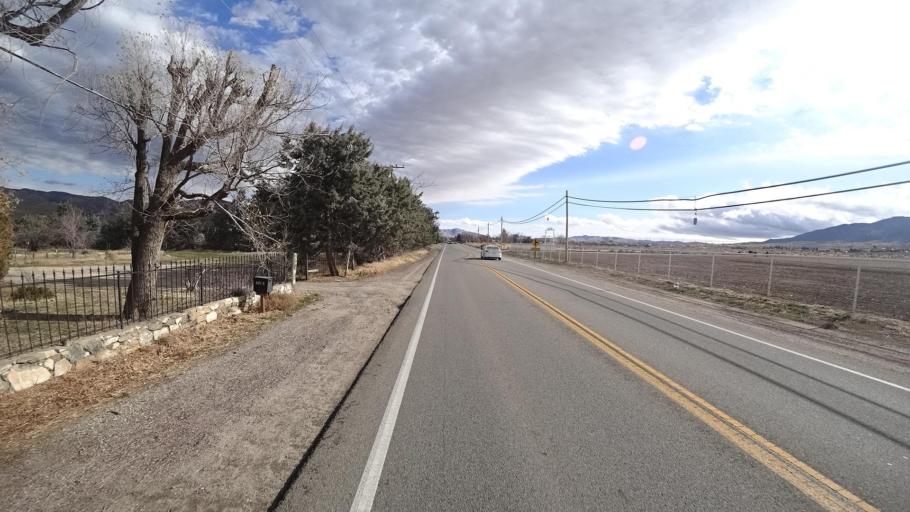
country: US
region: California
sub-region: Kern County
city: Golden Hills
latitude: 35.1244
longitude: -118.4751
